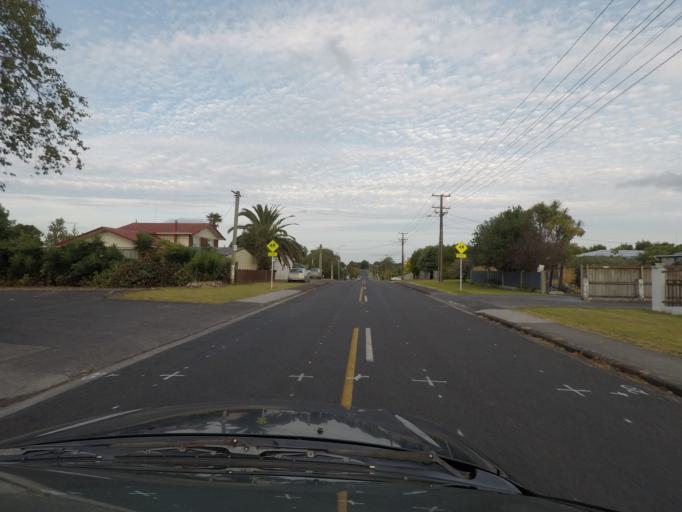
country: NZ
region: Auckland
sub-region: Auckland
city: Rosebank
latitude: -36.8316
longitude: 174.6498
